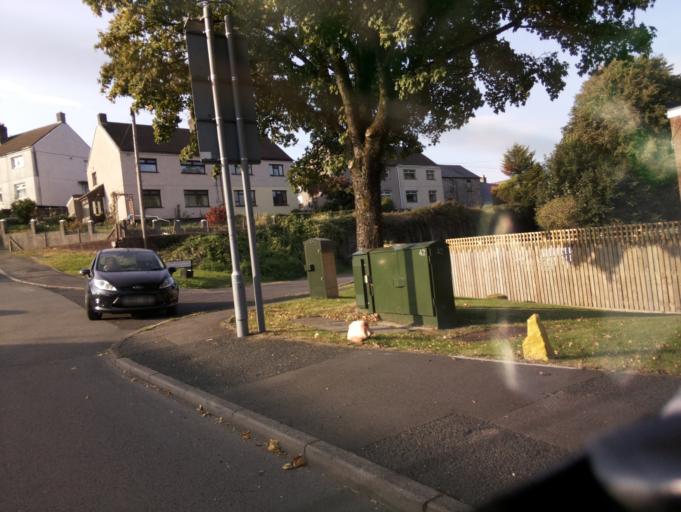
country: GB
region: Wales
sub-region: Torfaen County Borough
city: Pontypool
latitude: 51.6939
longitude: -3.0360
